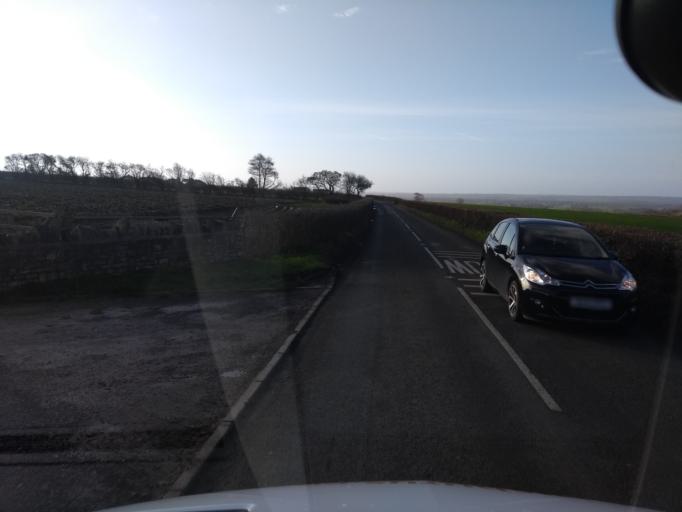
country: GB
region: England
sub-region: Somerset
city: Wedmore
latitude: 51.2156
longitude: -2.7985
